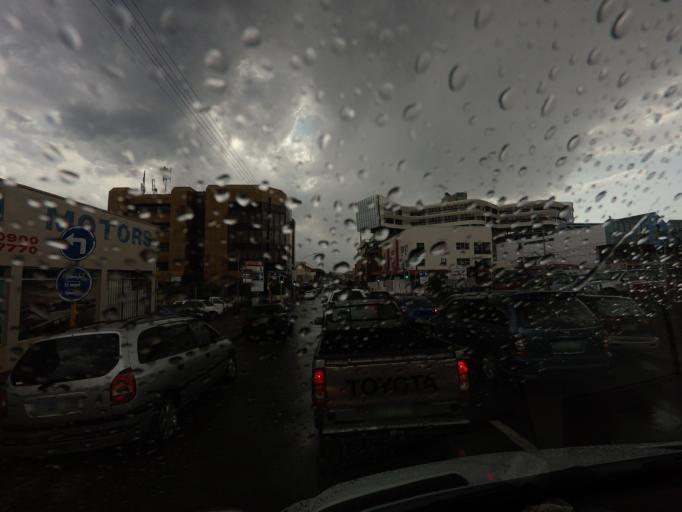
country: SZ
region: Manzini
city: Manzini
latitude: -26.4953
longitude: 31.3831
